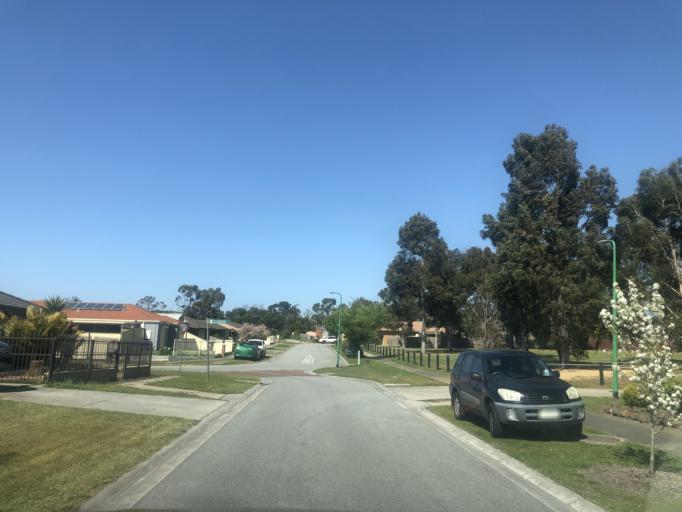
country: AU
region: Victoria
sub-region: Casey
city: Lynbrook
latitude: -38.0501
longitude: 145.2728
